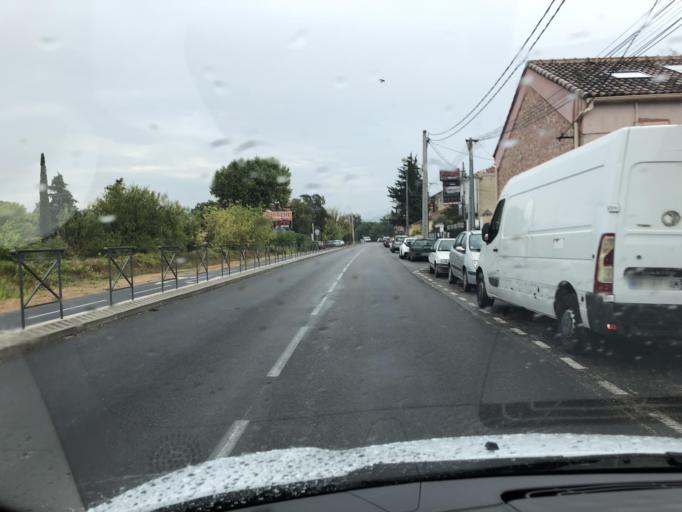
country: FR
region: Provence-Alpes-Cote d'Azur
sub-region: Departement des Bouches-du-Rhone
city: La Penne-sur-Huveaune
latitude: 43.2882
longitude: 5.5425
